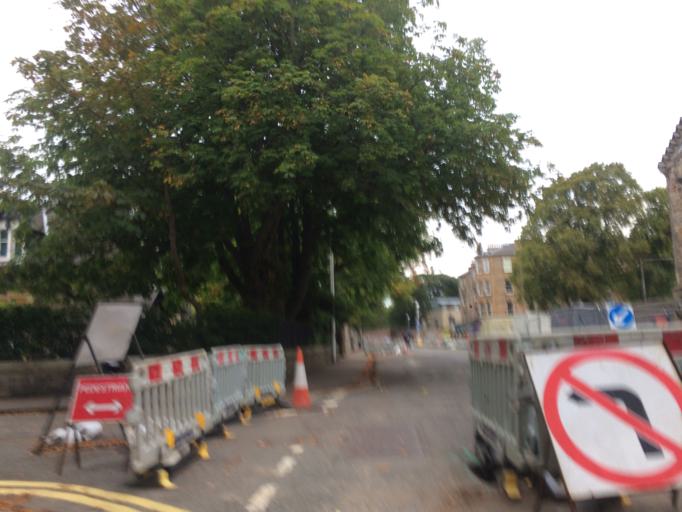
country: GB
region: Scotland
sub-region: Edinburgh
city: Edinburgh
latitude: 55.9345
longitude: -3.2012
